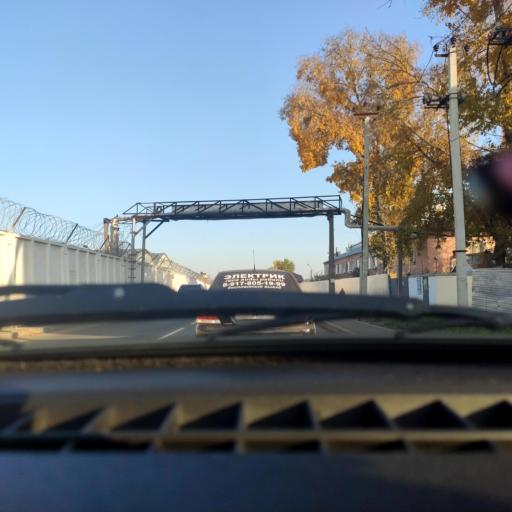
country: RU
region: Bashkortostan
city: Ufa
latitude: 54.7850
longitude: 56.0684
